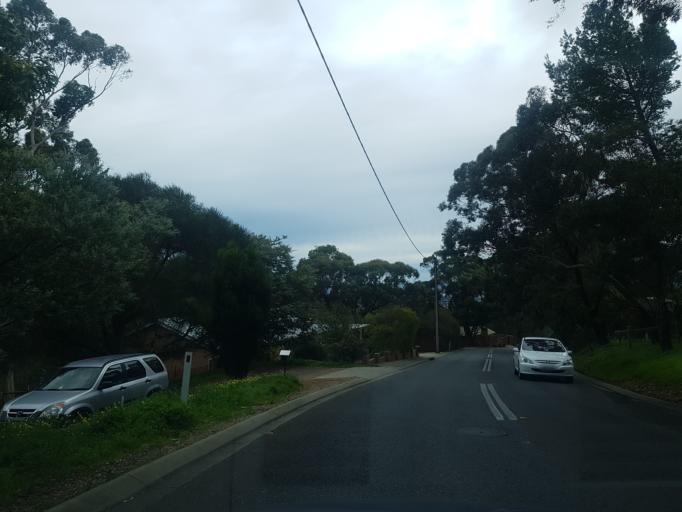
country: AU
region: South Australia
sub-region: Mitcham
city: Belair
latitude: -34.9957
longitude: 138.6248
